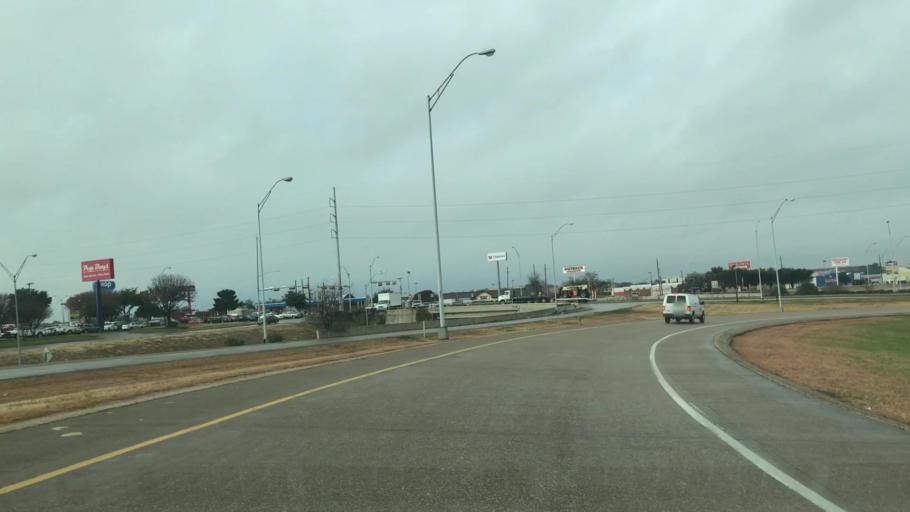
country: US
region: Texas
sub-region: Dallas County
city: Irving
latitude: 32.8358
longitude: -96.9921
